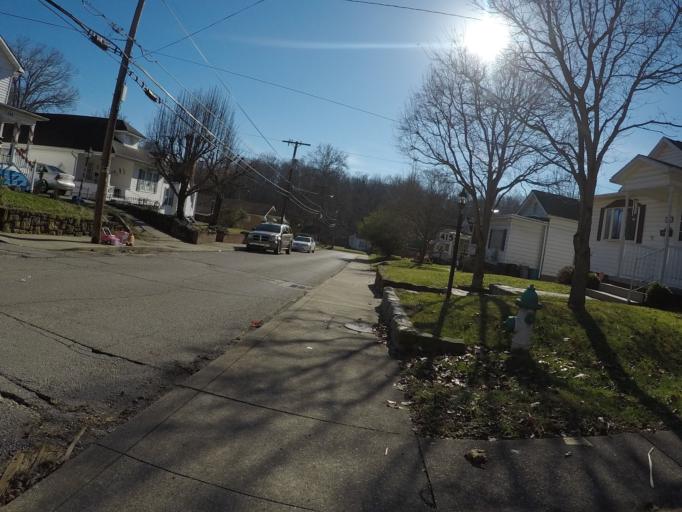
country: US
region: West Virginia
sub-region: Cabell County
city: Huntington
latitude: 38.4103
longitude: -82.3982
